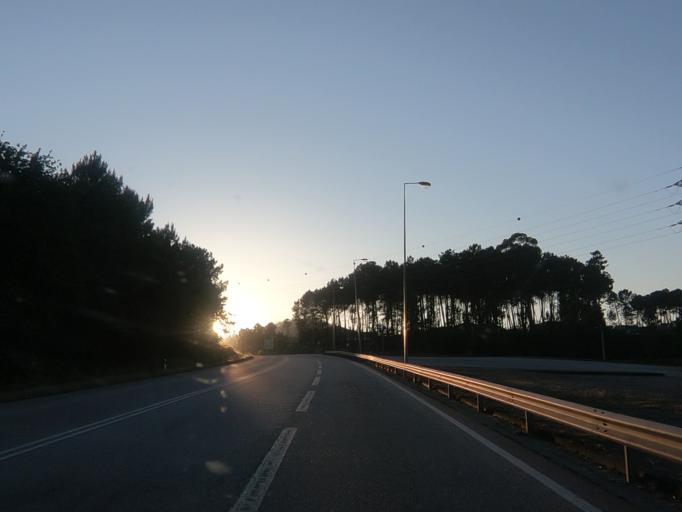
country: PT
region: Viseu
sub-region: Viseu
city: Abraveses
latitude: 40.6899
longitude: -7.9042
